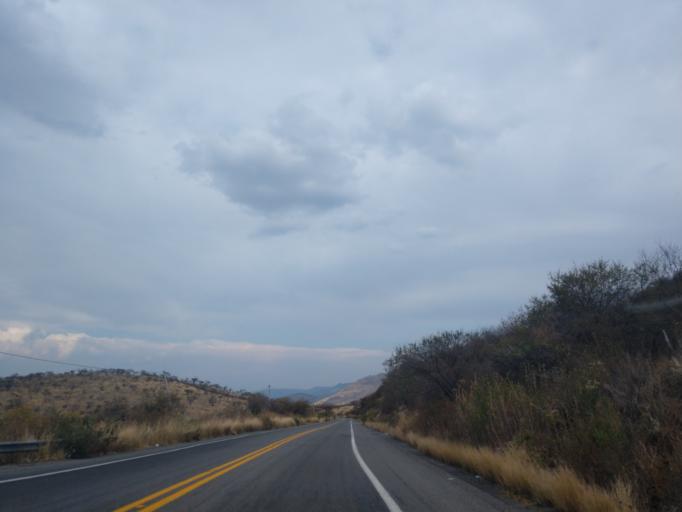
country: MX
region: Jalisco
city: La Manzanilla de la Paz
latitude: 20.1053
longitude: -103.1667
